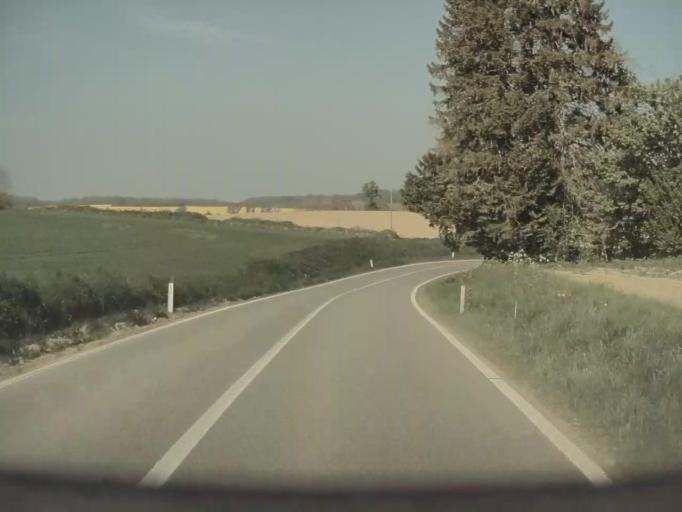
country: BE
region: Wallonia
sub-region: Province de Namur
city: Havelange
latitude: 50.3238
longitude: 5.2482
